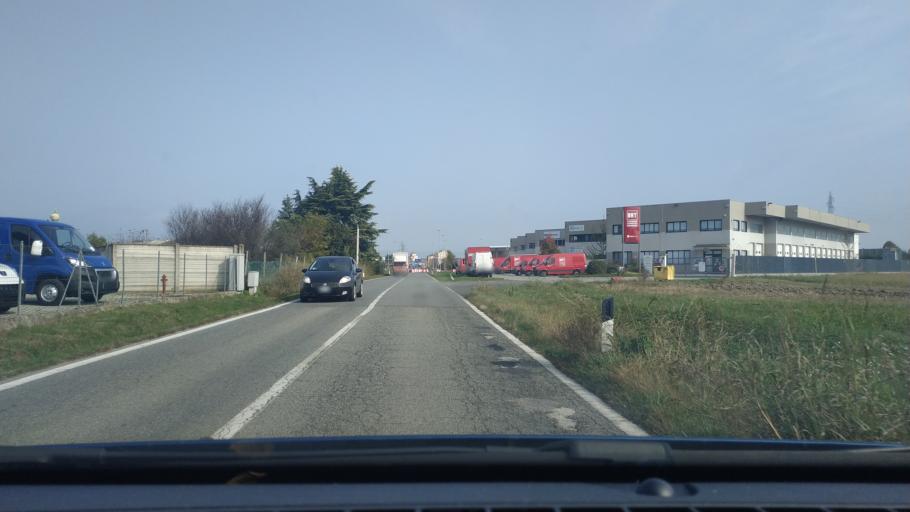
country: IT
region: Piedmont
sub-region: Provincia di Torino
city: Scarmagno
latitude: 45.3732
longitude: 7.8519
